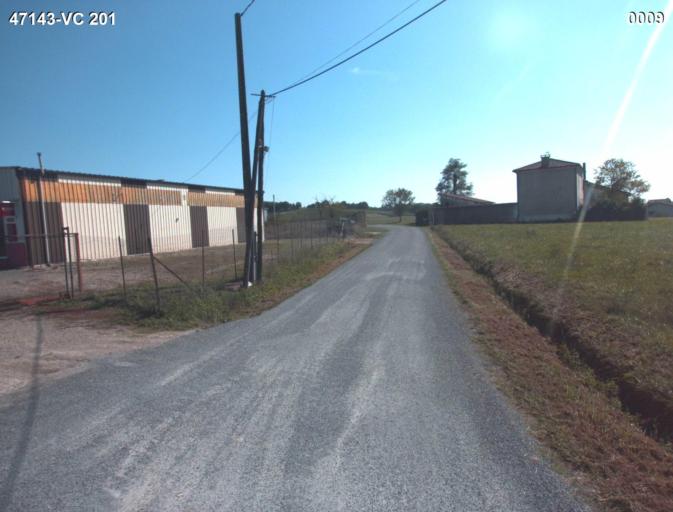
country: FR
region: Aquitaine
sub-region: Departement du Lot-et-Garonne
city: Lavardac
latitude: 44.1830
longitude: 0.3088
